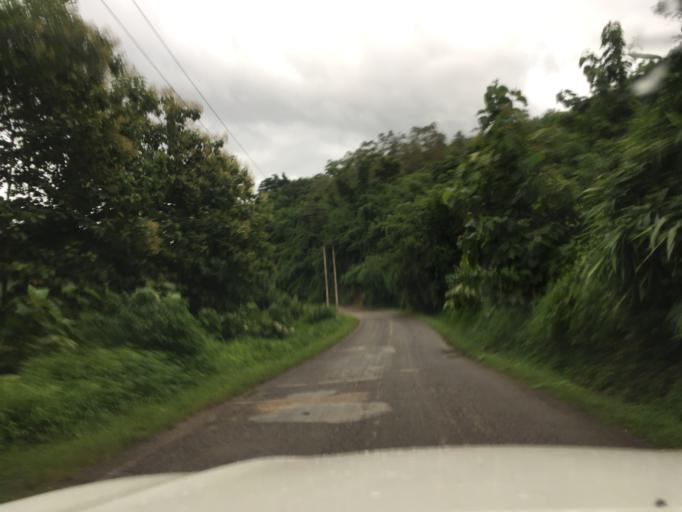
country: LA
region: Oudomxai
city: Muang La
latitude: 20.9657
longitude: 102.2211
